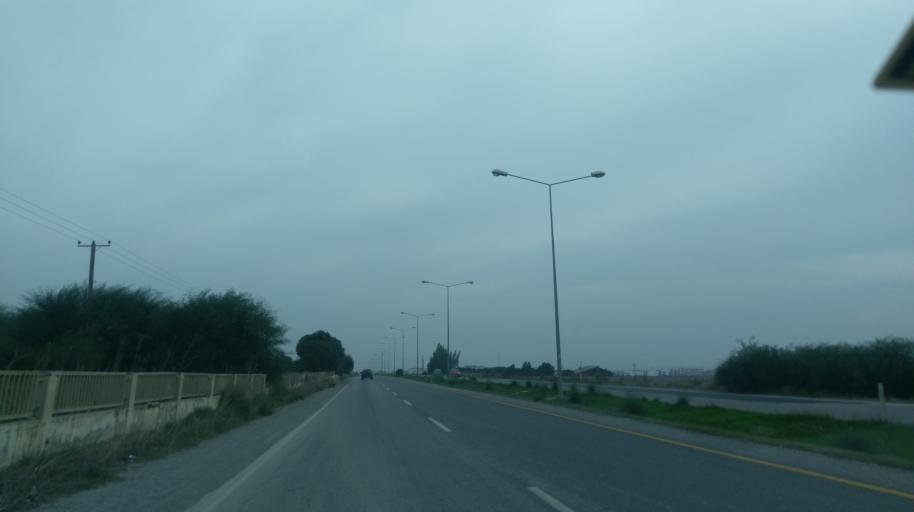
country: CY
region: Lefkosia
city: Mammari
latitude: 35.2124
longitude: 33.2560
